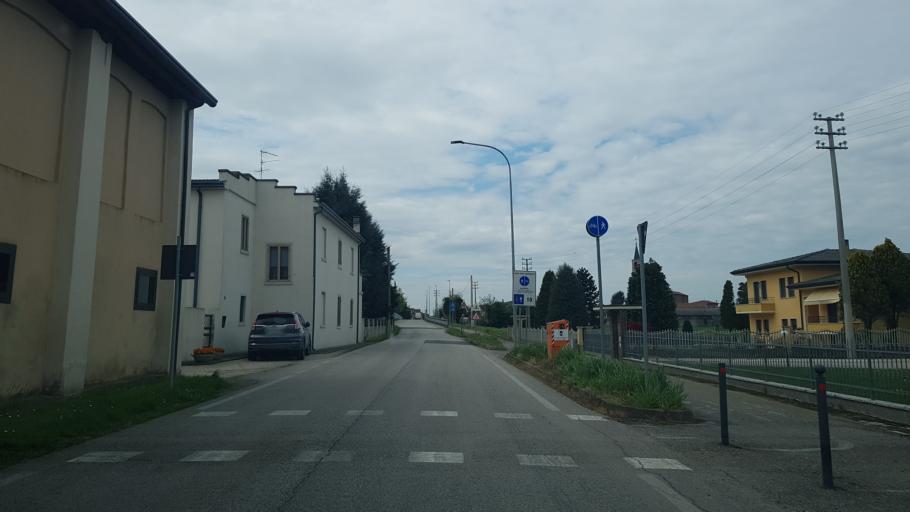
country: IT
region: Veneto
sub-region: Provincia di Padova
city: Piacenza d'Adige
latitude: 45.1260
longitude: 11.5526
